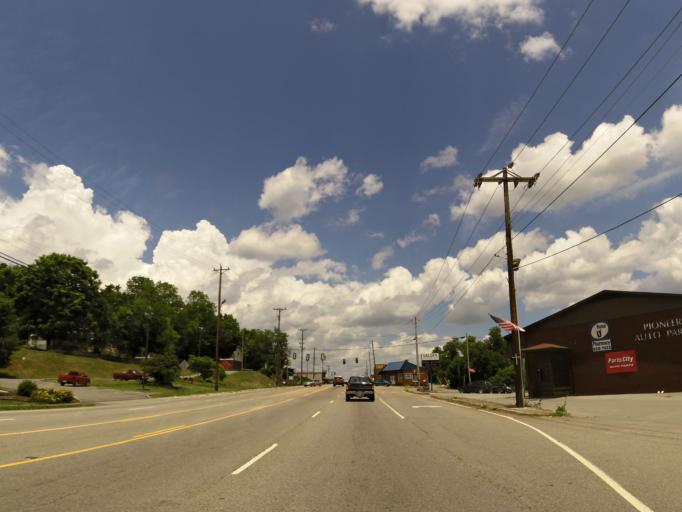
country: US
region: Tennessee
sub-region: Claiborne County
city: Tazewell
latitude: 36.4509
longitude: -83.5695
